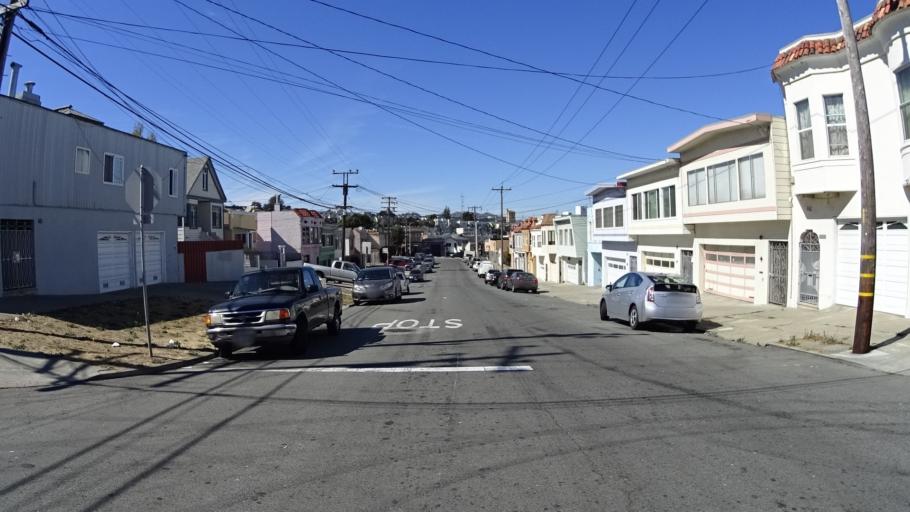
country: US
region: California
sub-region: San Mateo County
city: Brisbane
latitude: 37.7202
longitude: -122.3949
